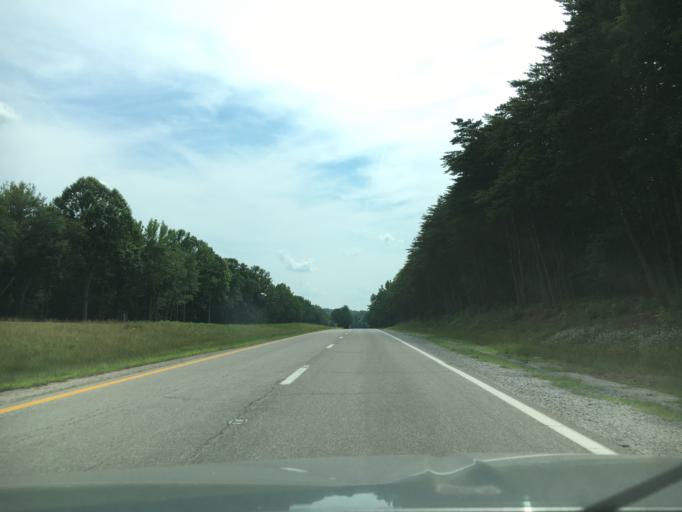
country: US
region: Virginia
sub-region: Lunenburg County
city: Victoria
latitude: 37.1186
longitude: -78.3391
